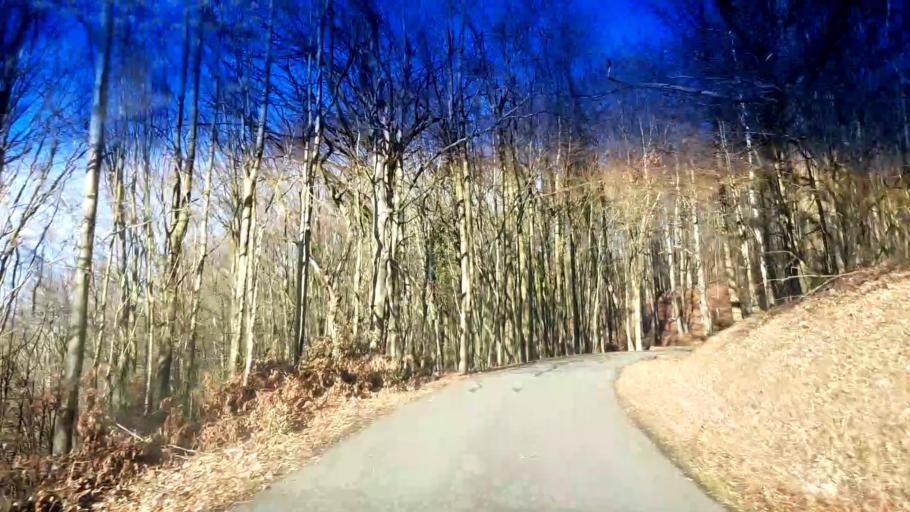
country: DE
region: Bavaria
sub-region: Upper Franconia
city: Buttenheim
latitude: 49.8351
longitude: 11.0796
